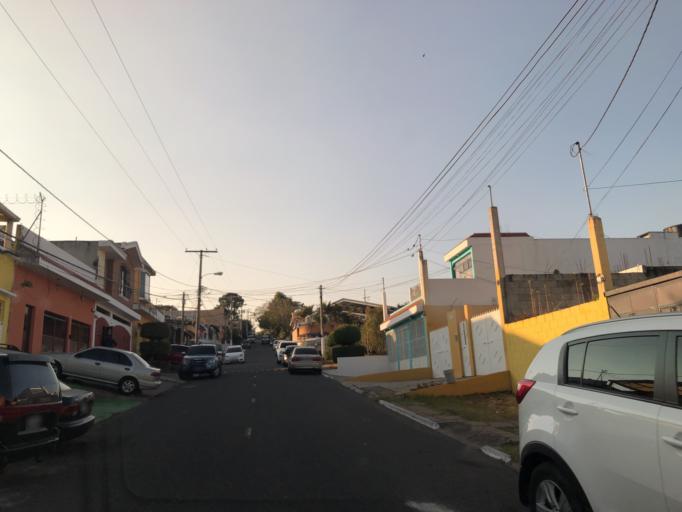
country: GT
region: Guatemala
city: Mixco
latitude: 14.6256
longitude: -90.5926
